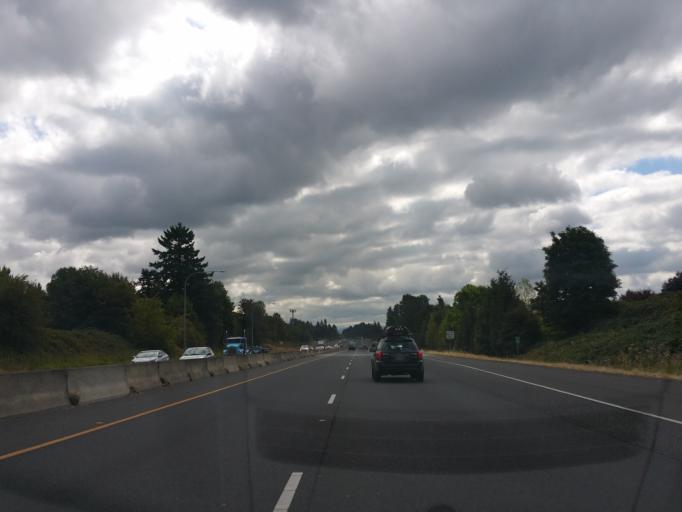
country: US
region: Washington
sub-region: Clark County
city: Mill Plain
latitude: 45.5948
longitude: -122.5154
